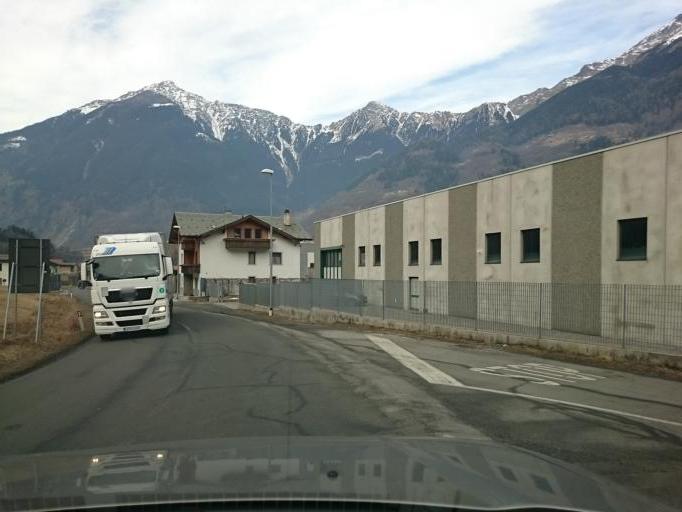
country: IT
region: Lombardy
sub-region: Provincia di Sondrio
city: Sondalo
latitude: 46.3258
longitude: 10.3316
